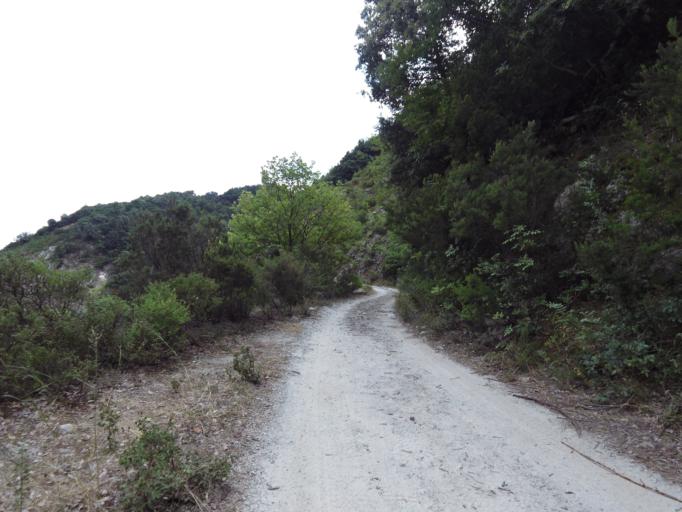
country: IT
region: Calabria
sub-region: Provincia di Reggio Calabria
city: Bivongi
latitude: 38.4967
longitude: 16.3993
